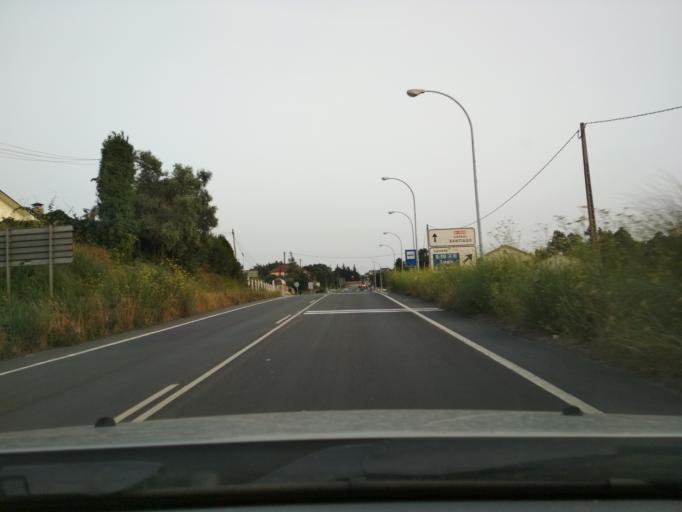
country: ES
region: Galicia
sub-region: Provincia da Coruna
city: Cambre
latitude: 43.2781
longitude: -8.3654
